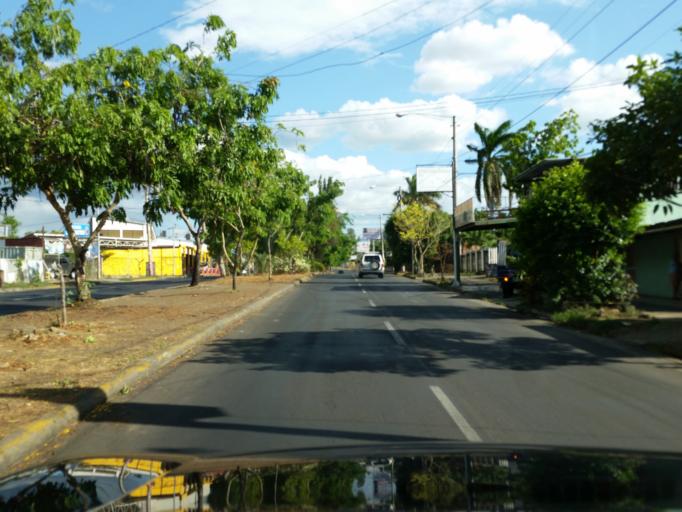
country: NI
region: Managua
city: Managua
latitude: 12.1300
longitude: -86.2751
